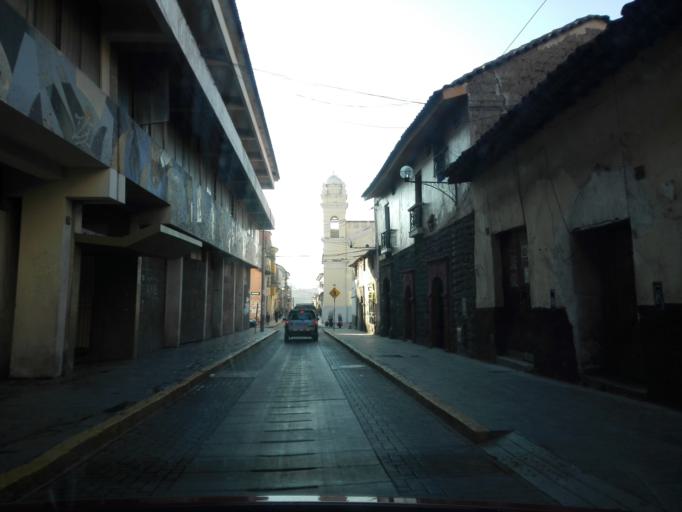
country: PE
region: Ayacucho
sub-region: Provincia de Huamanga
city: Ayacucho
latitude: -13.1612
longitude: -74.2246
